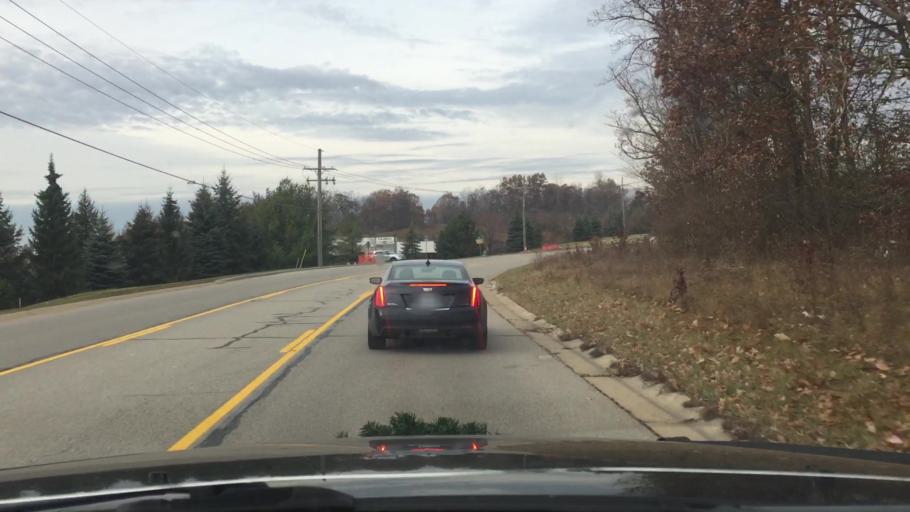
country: US
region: Michigan
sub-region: Oakland County
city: Auburn Hills
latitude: 42.7004
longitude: -83.2526
